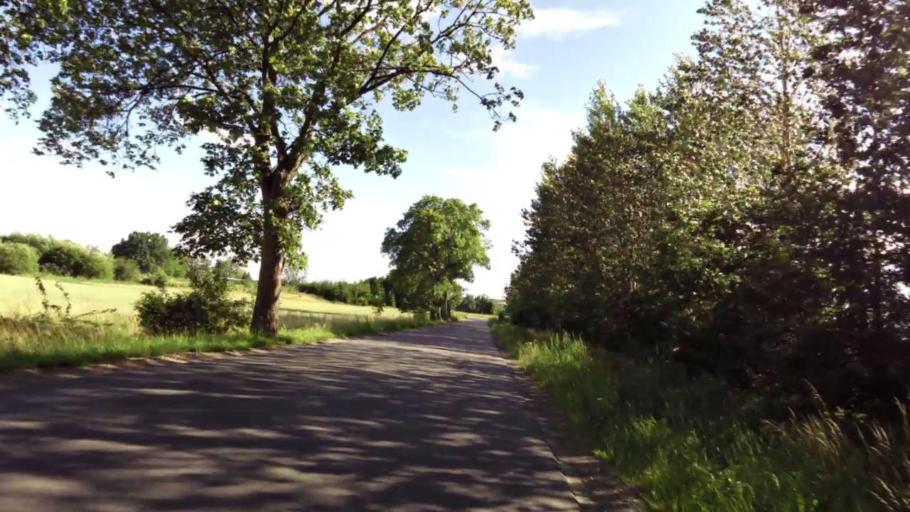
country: PL
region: West Pomeranian Voivodeship
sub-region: Powiat slawienski
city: Slawno
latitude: 54.4385
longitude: 16.7330
